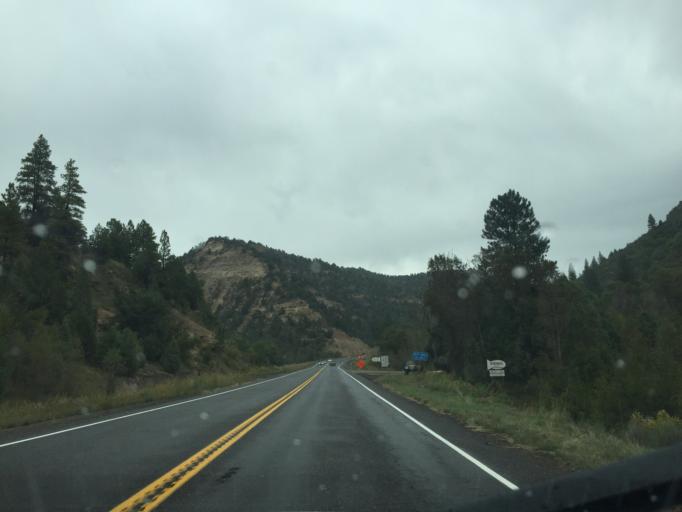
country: US
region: Utah
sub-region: Kane County
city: Kanab
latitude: 37.3744
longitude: -112.5940
